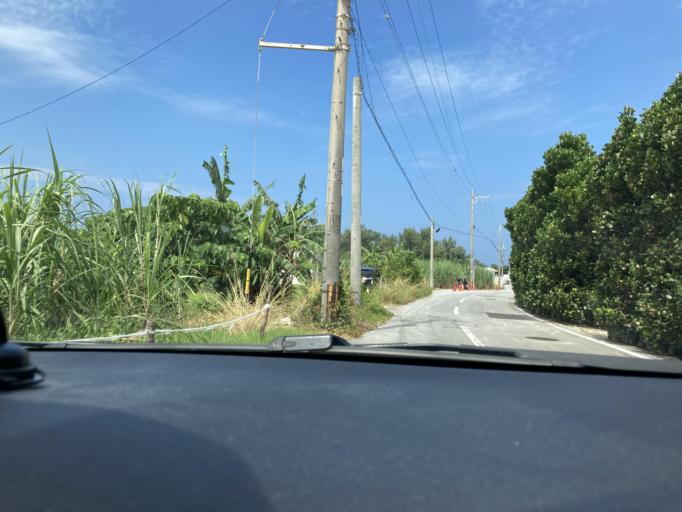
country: JP
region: Okinawa
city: Ishikawa
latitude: 26.4413
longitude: 127.7711
